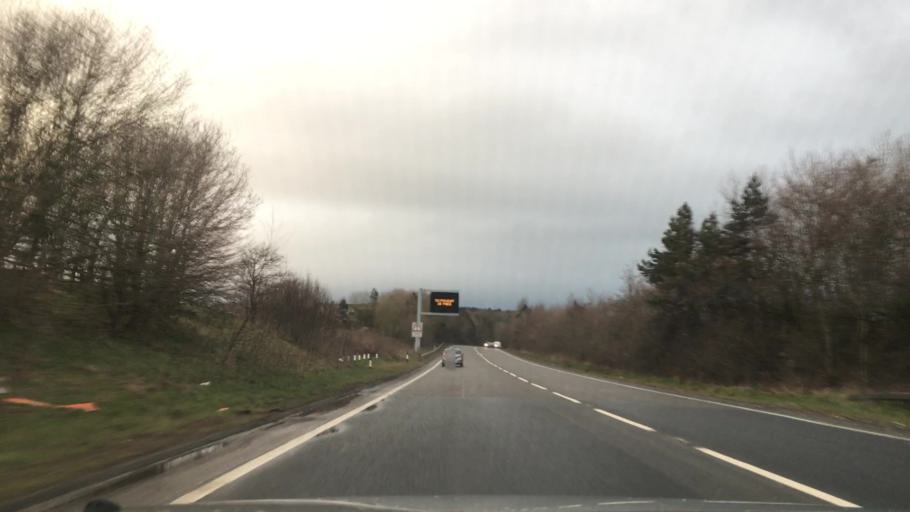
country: GB
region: England
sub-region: Cumbria
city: Askam in Furness
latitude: 54.1584
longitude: -3.2078
